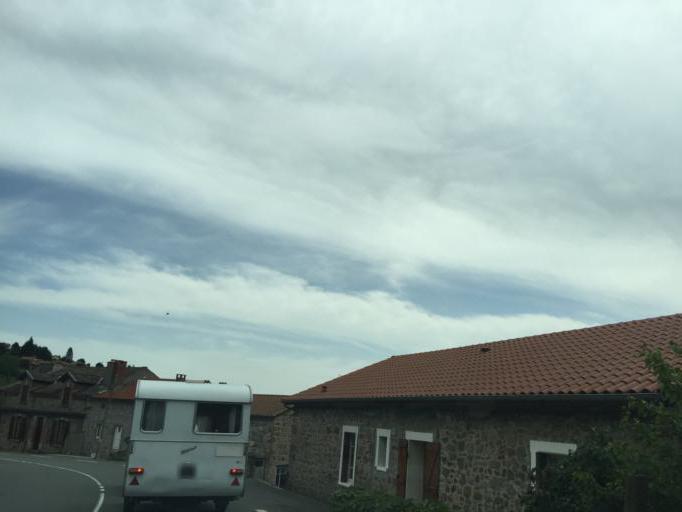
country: FR
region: Rhone-Alpes
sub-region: Departement de la Loire
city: Bourg-Argental
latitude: 45.3159
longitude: 4.5259
